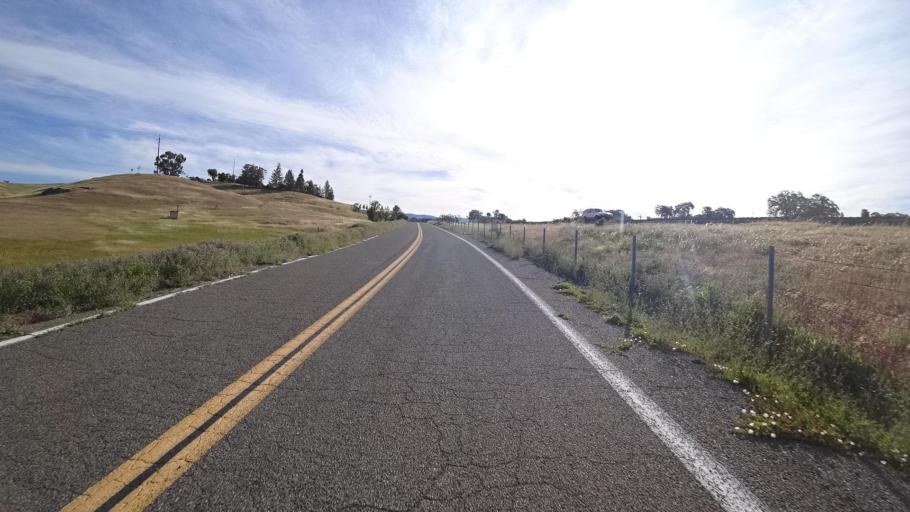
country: US
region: California
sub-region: Lake County
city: North Lakeport
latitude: 39.0881
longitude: -122.9211
